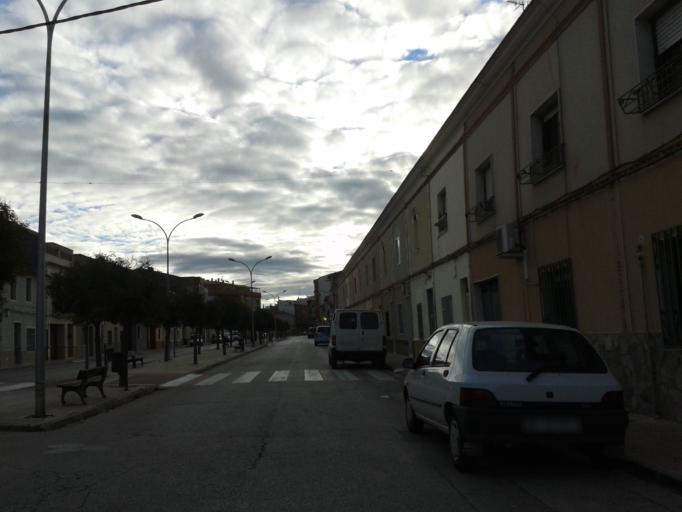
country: ES
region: Castille-La Mancha
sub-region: Provincia de Albacete
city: Caudete
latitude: 38.7100
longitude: -0.9837
